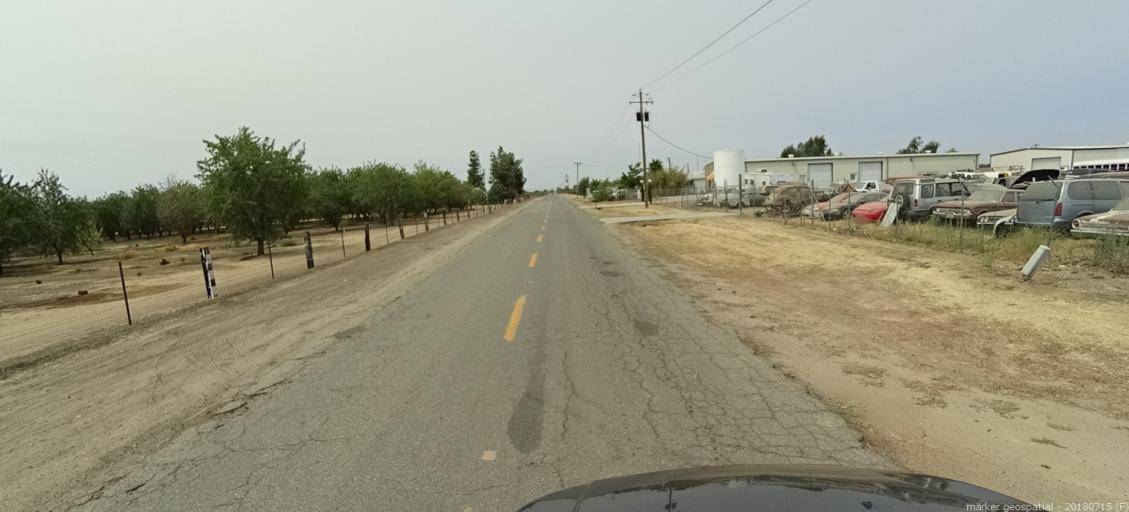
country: US
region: California
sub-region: Madera County
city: Madera Acres
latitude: 37.0096
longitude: -120.1105
